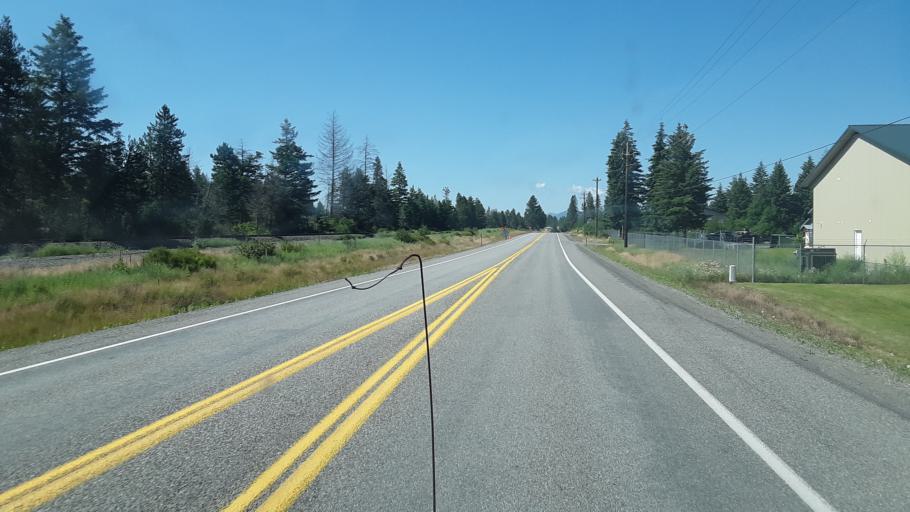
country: US
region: Idaho
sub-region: Kootenai County
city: Hayden
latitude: 47.8298
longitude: -116.7810
